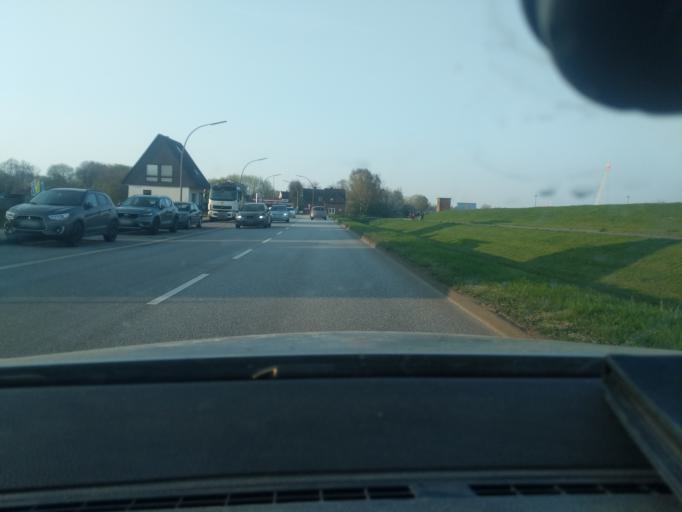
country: DE
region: Hamburg
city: Altona
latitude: 53.5247
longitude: 9.8869
